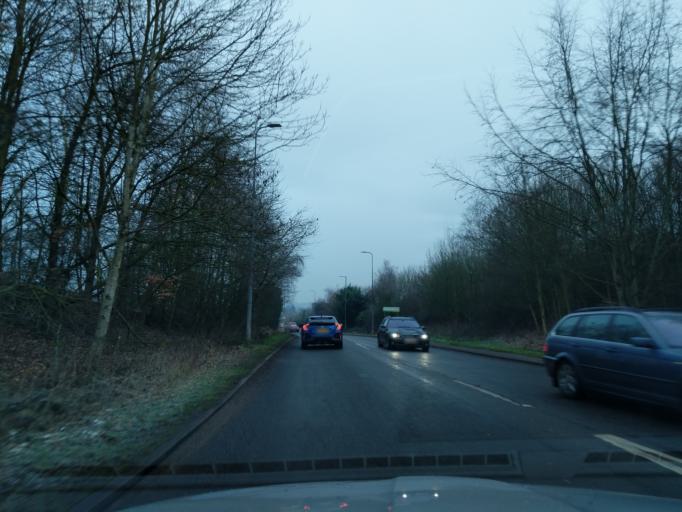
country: GB
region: England
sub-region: Hertfordshire
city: Kings Langley
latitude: 51.7014
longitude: -0.4444
